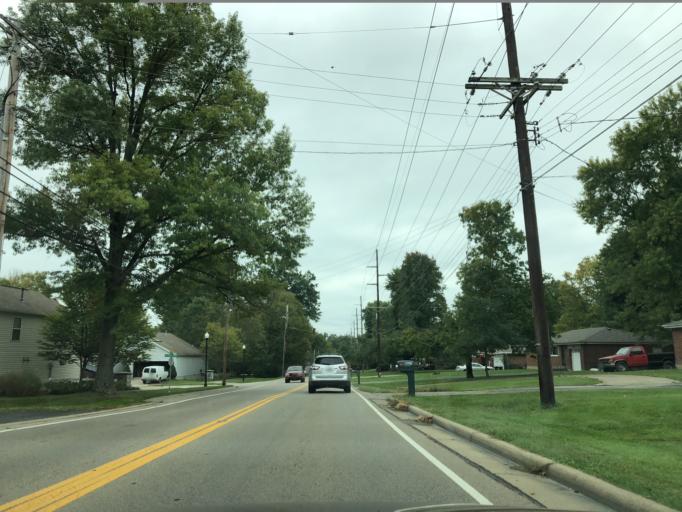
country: US
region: Ohio
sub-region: Warren County
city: Landen
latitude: 39.3043
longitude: -84.2788
